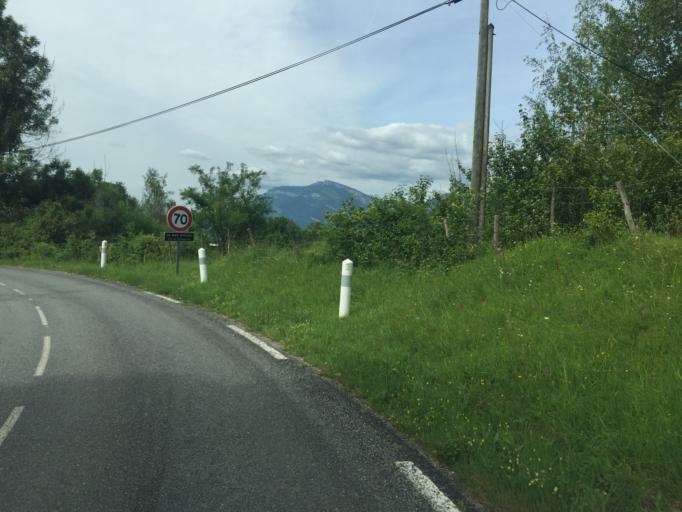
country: FR
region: Rhone-Alpes
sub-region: Departement de la Savoie
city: Jacob-Bellecombette
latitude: 45.5145
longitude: 5.9166
